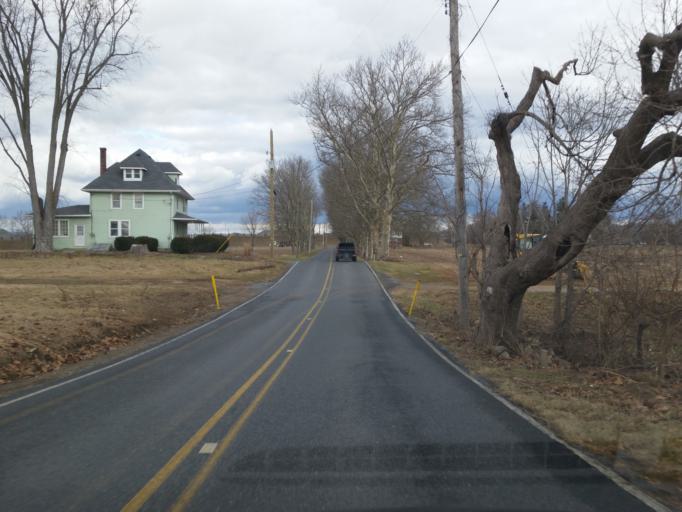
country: US
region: Pennsylvania
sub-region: Lebanon County
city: Annville
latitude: 40.3204
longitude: -76.5428
